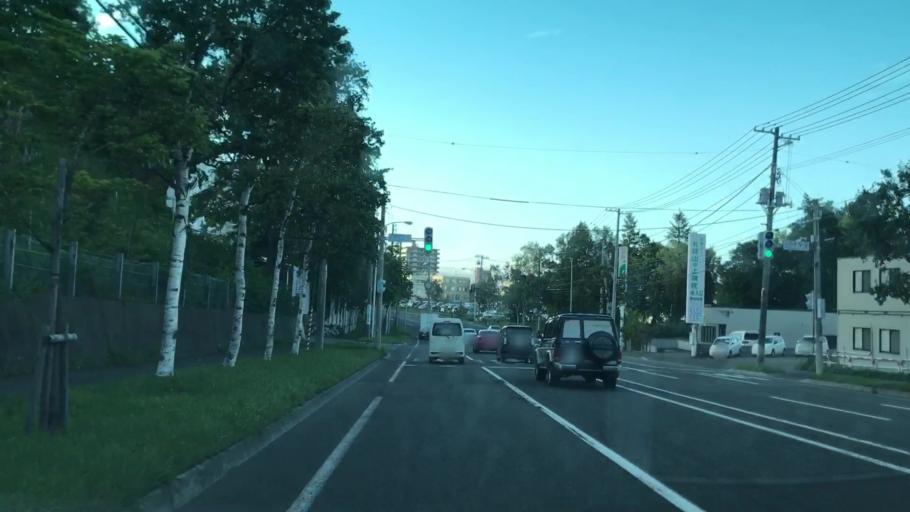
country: JP
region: Hokkaido
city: Sapporo
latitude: 43.0685
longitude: 141.2878
